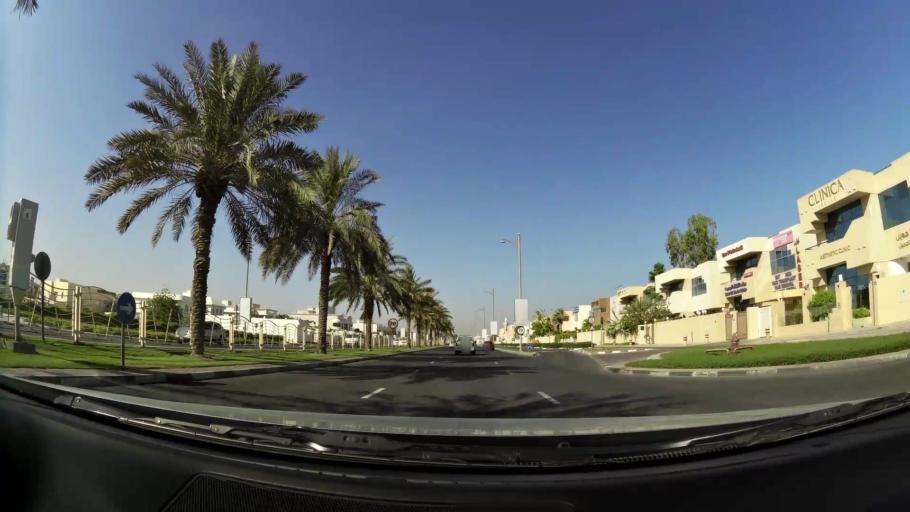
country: AE
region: Dubai
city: Dubai
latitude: 25.1828
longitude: 55.2259
